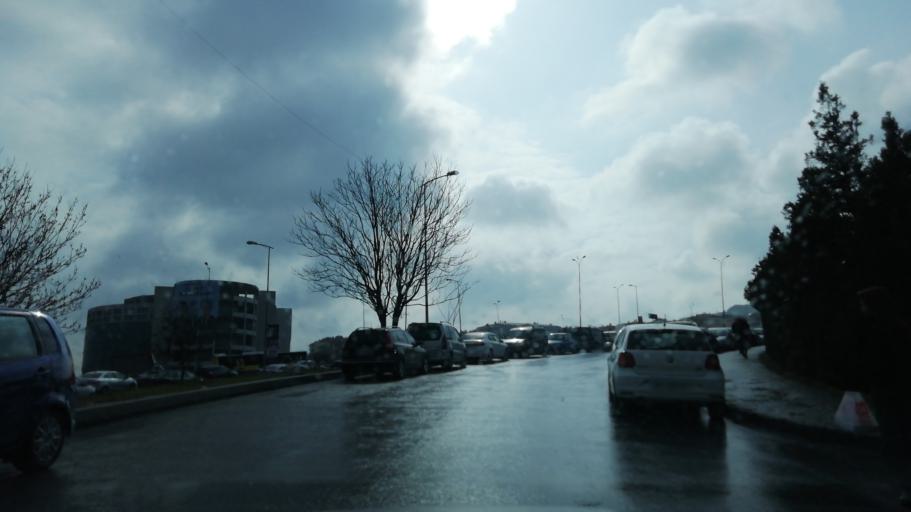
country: TR
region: Istanbul
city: Yakuplu
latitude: 41.0070
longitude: 28.6760
